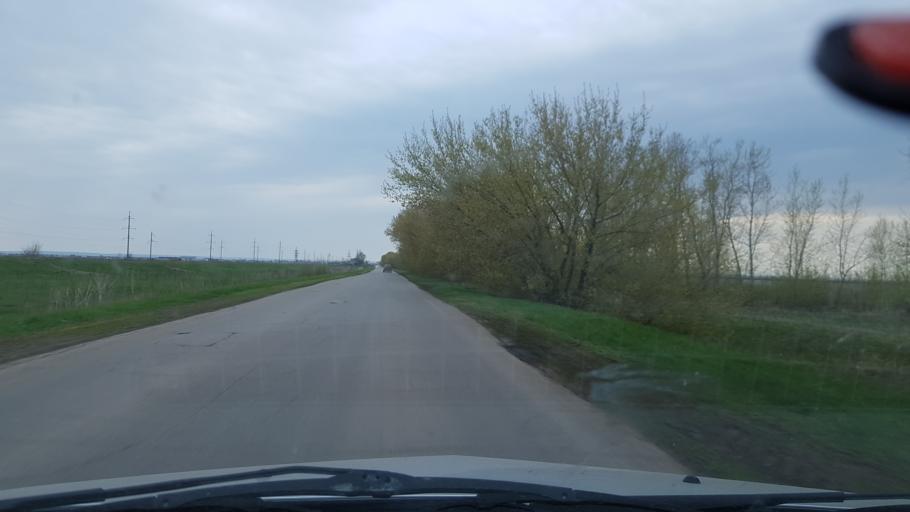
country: RU
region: Samara
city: Khryashchevka
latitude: 53.6697
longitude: 49.1212
